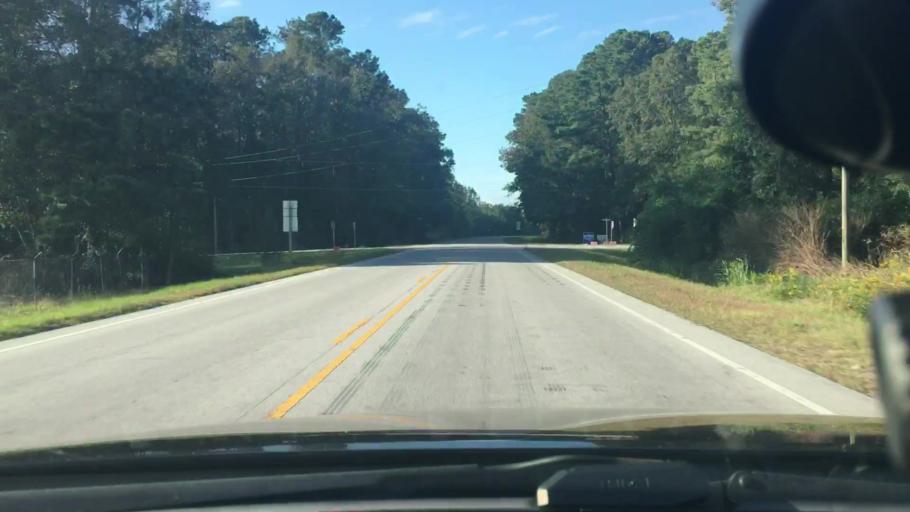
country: US
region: North Carolina
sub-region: Craven County
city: Vanceboro
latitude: 35.3188
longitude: -77.1441
